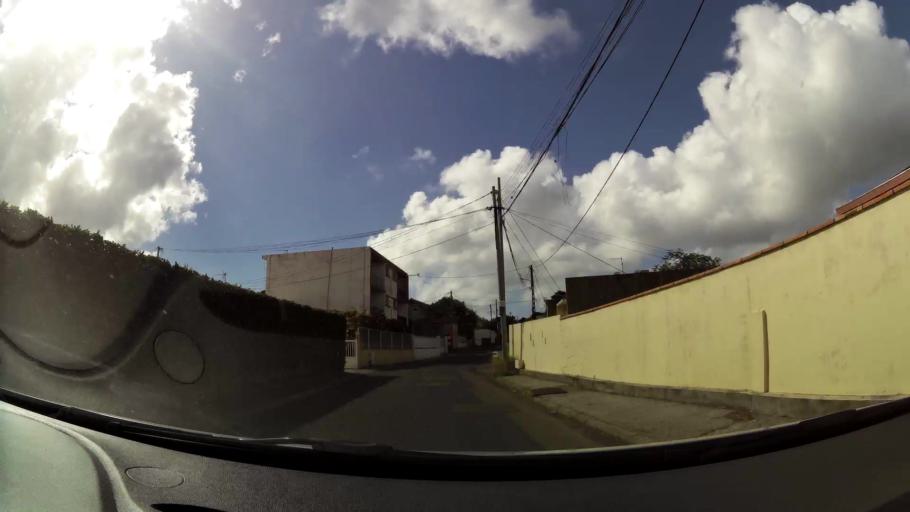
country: MQ
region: Martinique
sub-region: Martinique
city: Saint-Joseph
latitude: 14.6441
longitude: -61.0559
